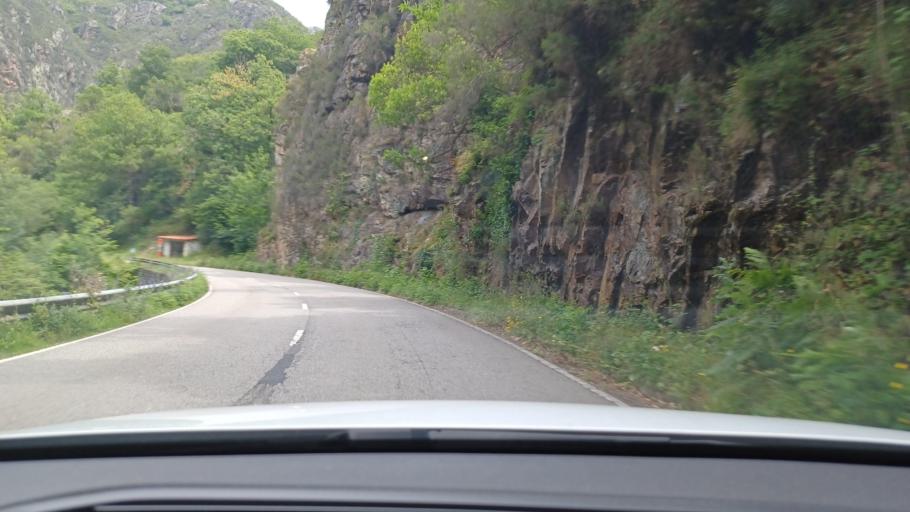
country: ES
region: Asturias
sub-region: Province of Asturias
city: Proaza
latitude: 43.2103
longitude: -6.0556
